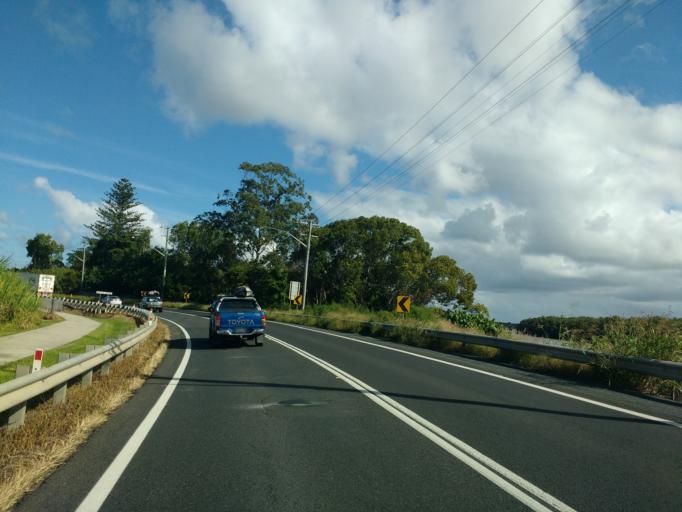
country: AU
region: New South Wales
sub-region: Richmond Valley
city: Evans Head
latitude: -29.0053
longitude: 153.4362
